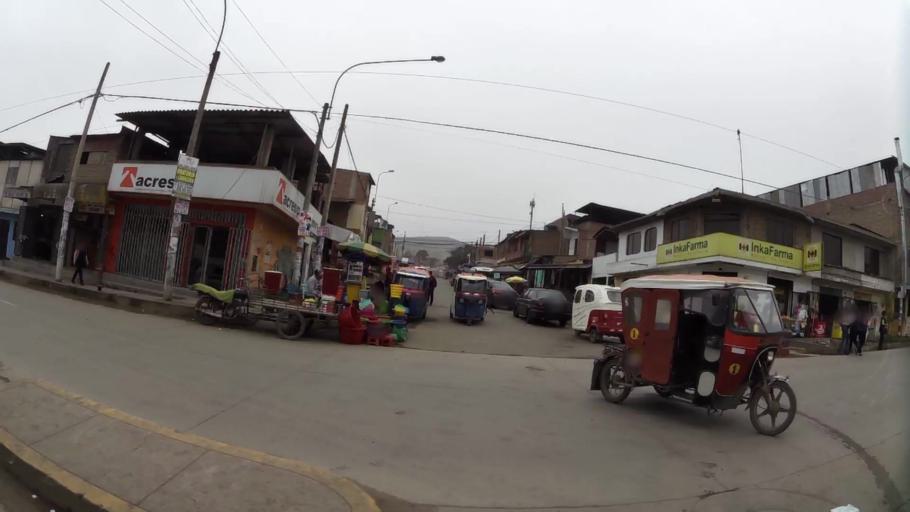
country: PE
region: Lima
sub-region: Lima
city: Surco
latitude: -12.1885
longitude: -76.9274
